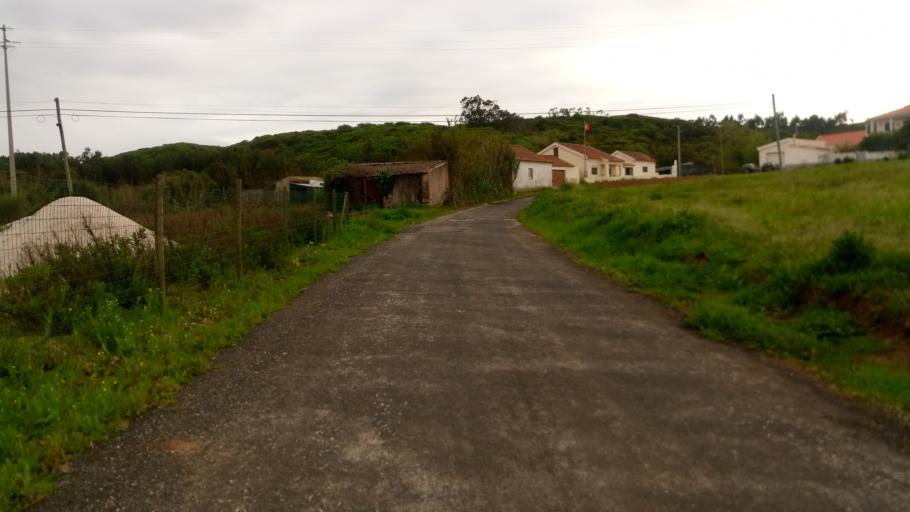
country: PT
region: Leiria
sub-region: Caldas da Rainha
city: Caldas da Rainha
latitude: 39.4527
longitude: -9.1862
